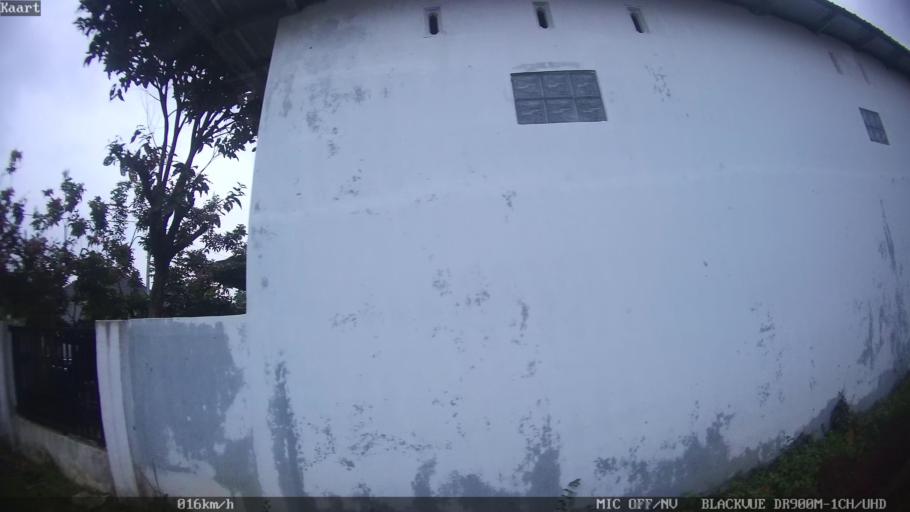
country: ID
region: Lampung
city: Bandarlampung
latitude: -5.4081
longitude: 105.2749
